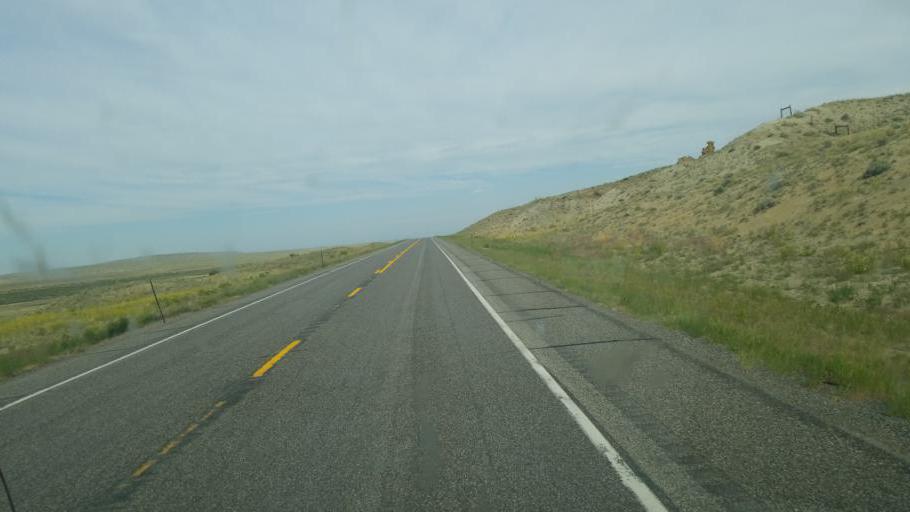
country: US
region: Wyoming
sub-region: Fremont County
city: Riverton
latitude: 43.2210
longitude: -107.9980
